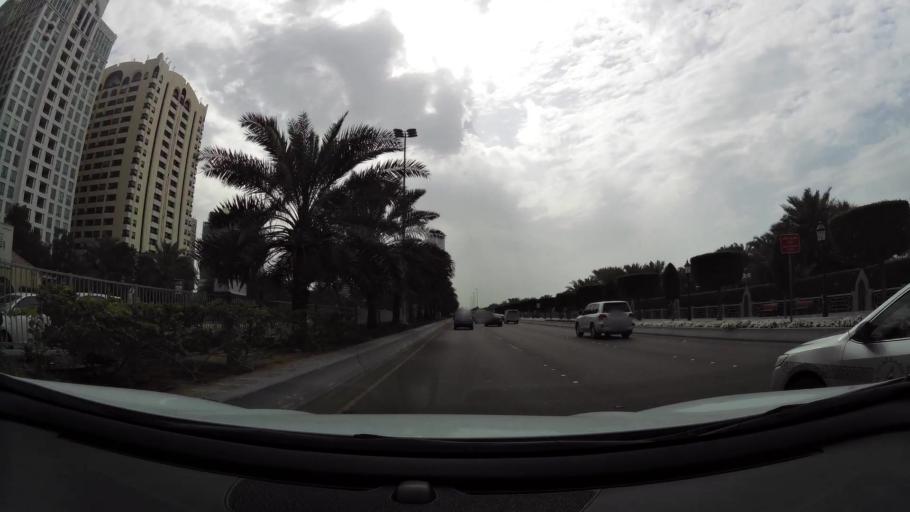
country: AE
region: Abu Dhabi
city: Abu Dhabi
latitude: 24.4722
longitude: 54.3395
